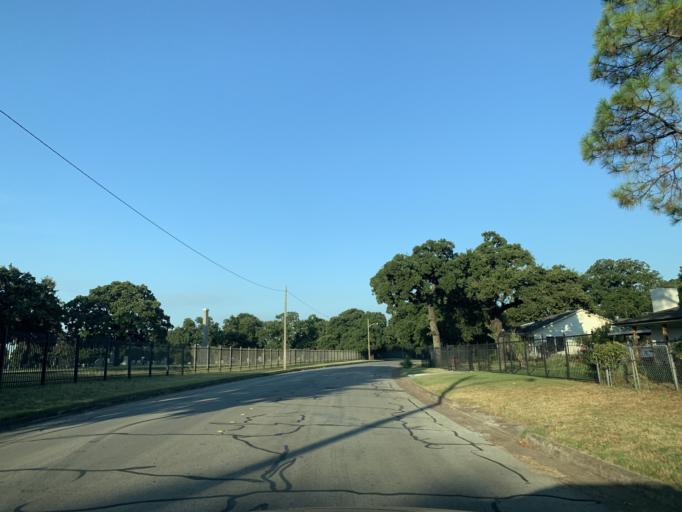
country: US
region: Texas
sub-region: Tarrant County
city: River Oaks
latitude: 32.7696
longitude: -97.3510
